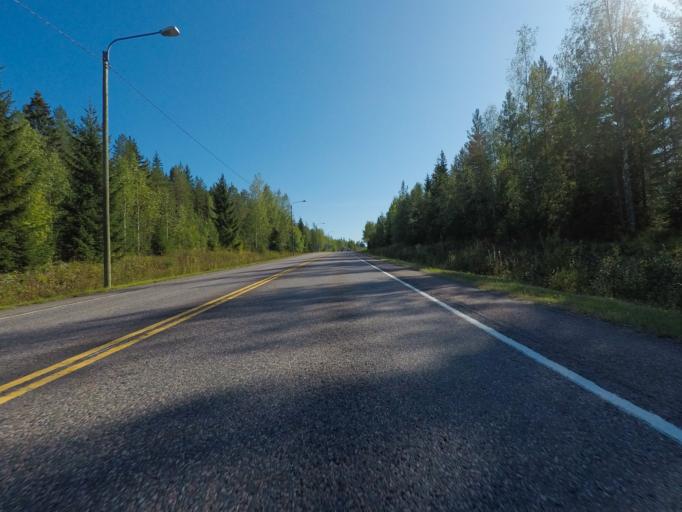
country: FI
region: Northern Savo
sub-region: Varkaus
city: Varkaus
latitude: 62.3484
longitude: 27.8190
